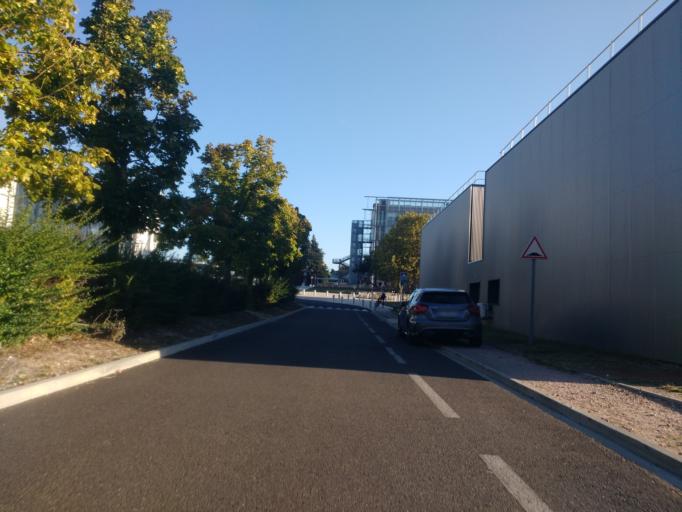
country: FR
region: Aquitaine
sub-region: Departement de la Gironde
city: Talence
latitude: 44.8080
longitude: -0.5981
